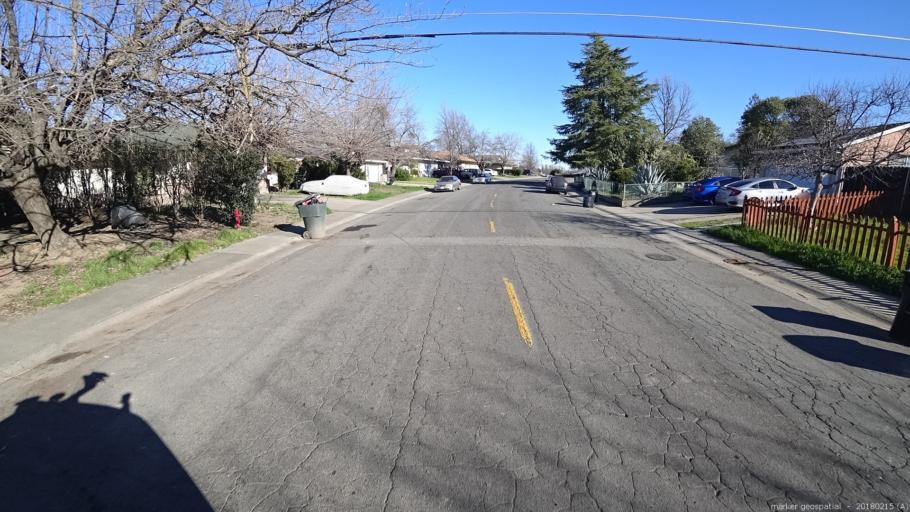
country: US
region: California
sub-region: Sacramento County
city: Foothill Farms
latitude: 38.6689
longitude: -121.3226
